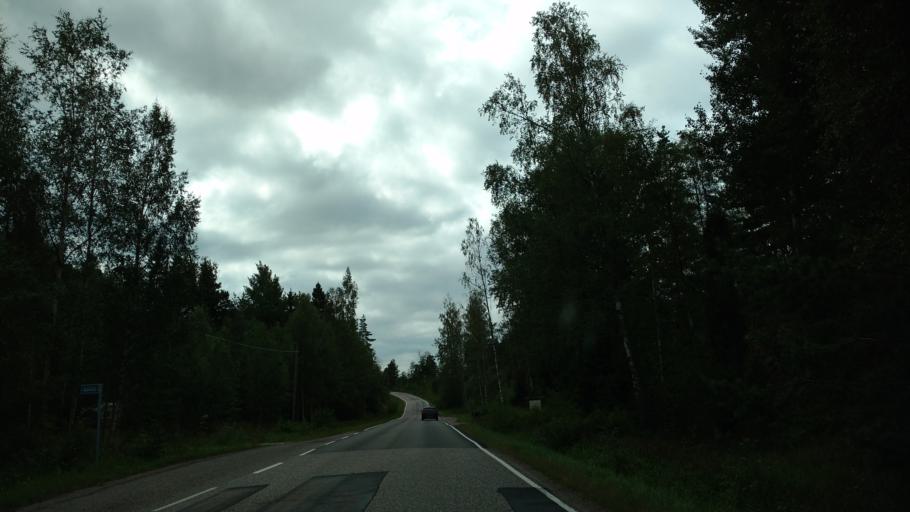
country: FI
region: Varsinais-Suomi
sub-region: Aboland-Turunmaa
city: Dragsfjaerd
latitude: 60.0108
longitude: 22.4555
